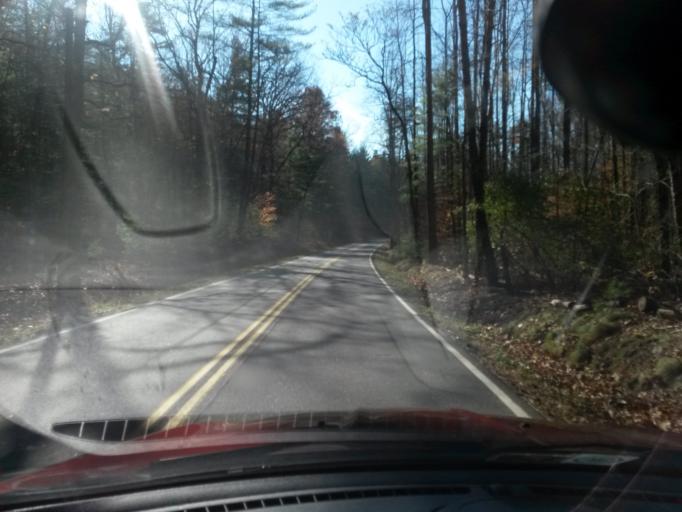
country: US
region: Virginia
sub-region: Botetourt County
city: Buchanan
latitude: 37.6287
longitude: -79.7337
